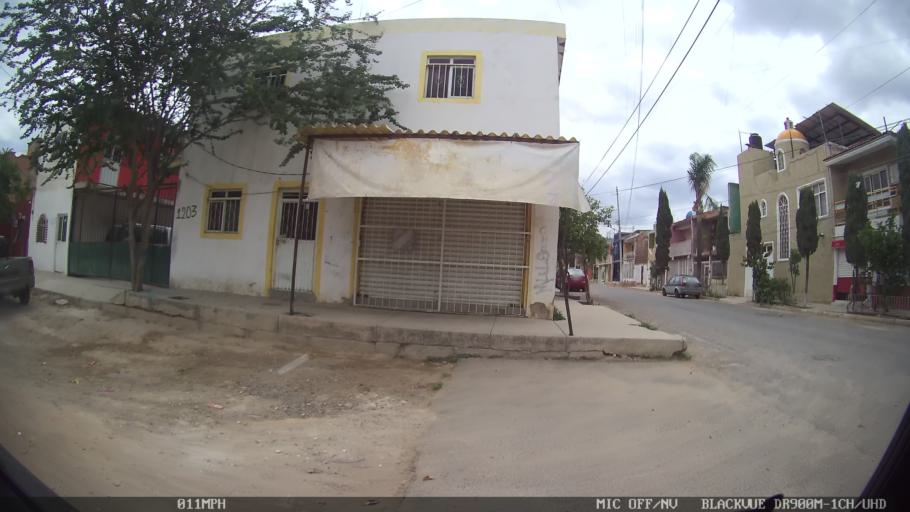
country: MX
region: Jalisco
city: Tonala
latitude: 20.6395
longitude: -103.2505
